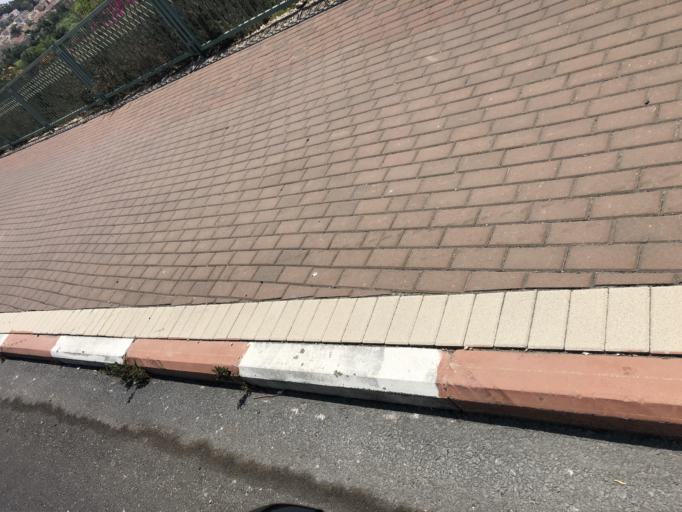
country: IL
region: Haifa
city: Daliyat el Karmil
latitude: 32.6360
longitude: 35.0809
